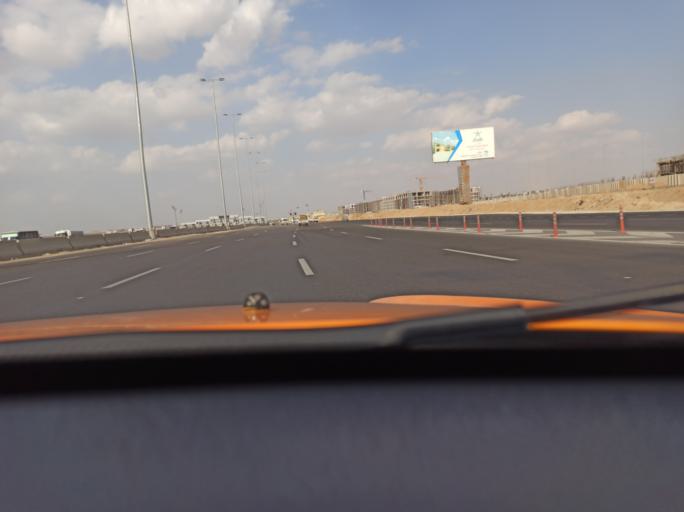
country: EG
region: Eastern Province
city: Bilbays
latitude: 30.2045
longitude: 31.6676
